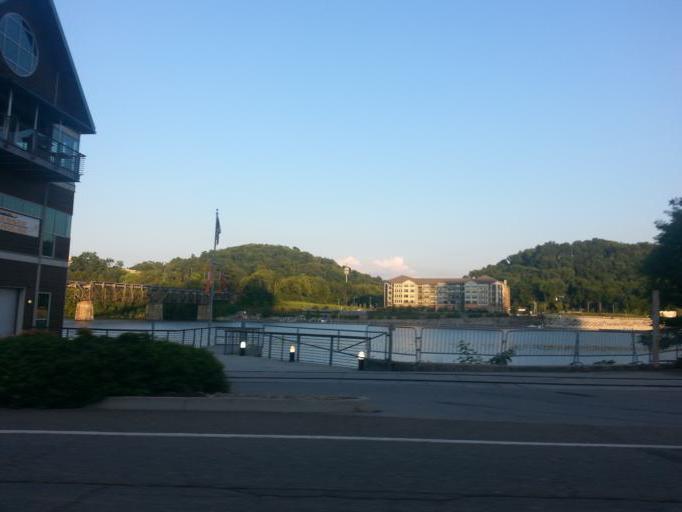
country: US
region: Tennessee
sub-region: Knox County
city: Knoxville
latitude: 35.9551
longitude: -83.9224
